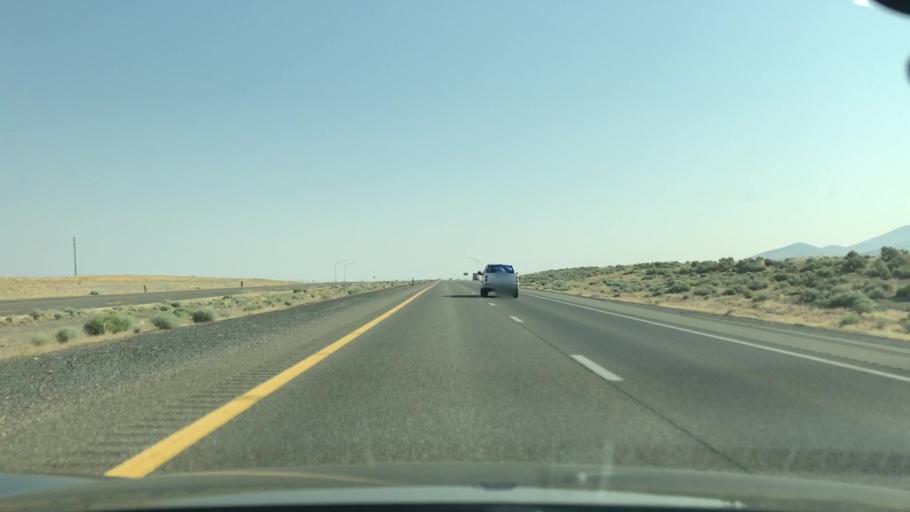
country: US
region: Nevada
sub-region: Humboldt County
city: Winnemucca
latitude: 40.7817
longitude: -118.0035
